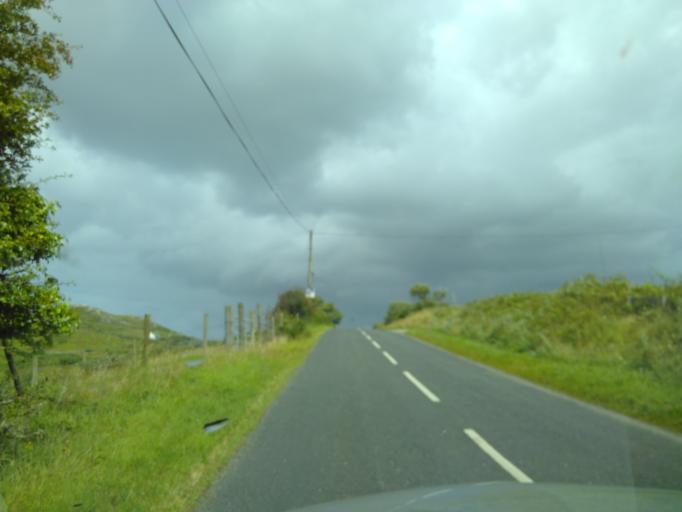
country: IE
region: Ulster
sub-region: County Donegal
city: Buncrana
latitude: 55.1727
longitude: -7.5819
